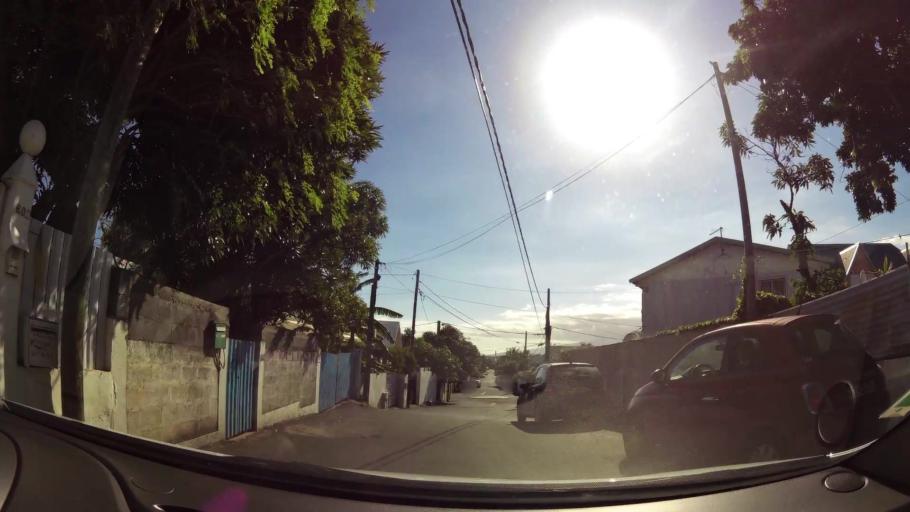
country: RE
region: Reunion
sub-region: Reunion
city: Saint-Pierre
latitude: -21.3465
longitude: 55.4851
